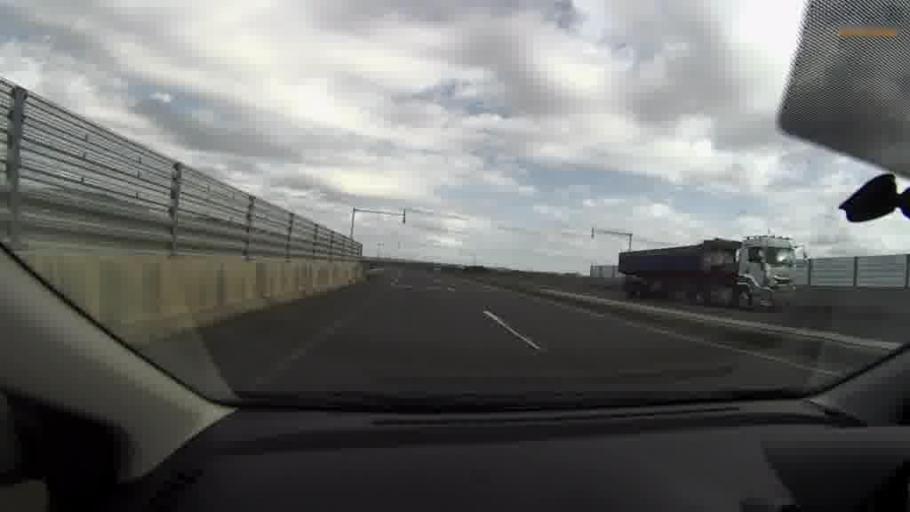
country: JP
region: Hokkaido
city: Kushiro
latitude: 43.0091
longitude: 144.2563
